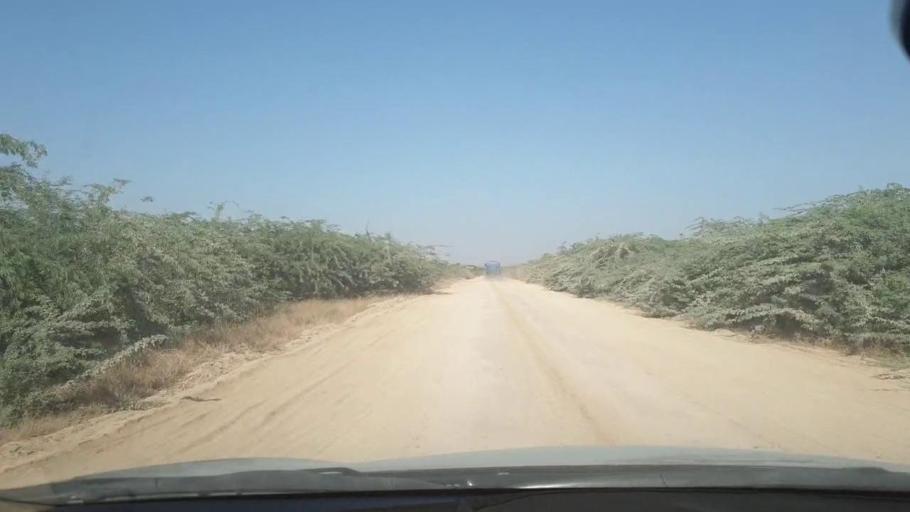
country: PK
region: Sindh
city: Malir Cantonment
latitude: 25.1436
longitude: 67.1653
